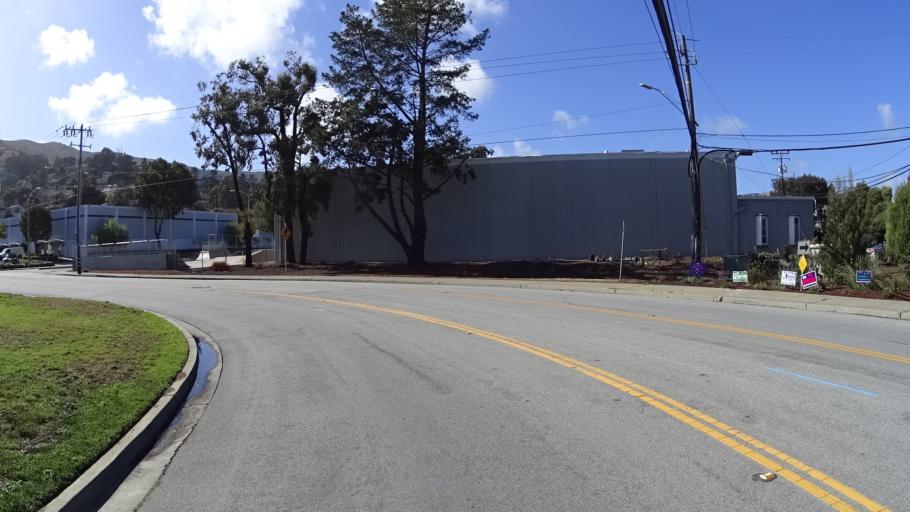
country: US
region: California
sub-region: San Mateo County
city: Brisbane
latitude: 37.6857
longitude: -122.4016
